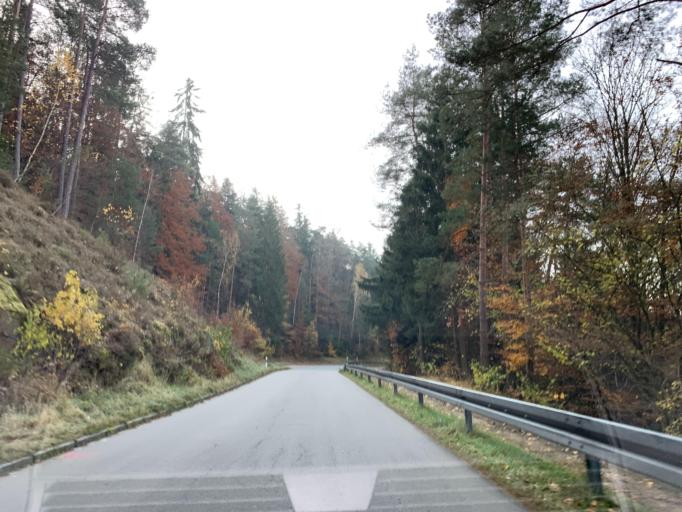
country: DE
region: Bavaria
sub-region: Upper Palatinate
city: Thanstein
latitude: 49.3540
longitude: 12.4494
